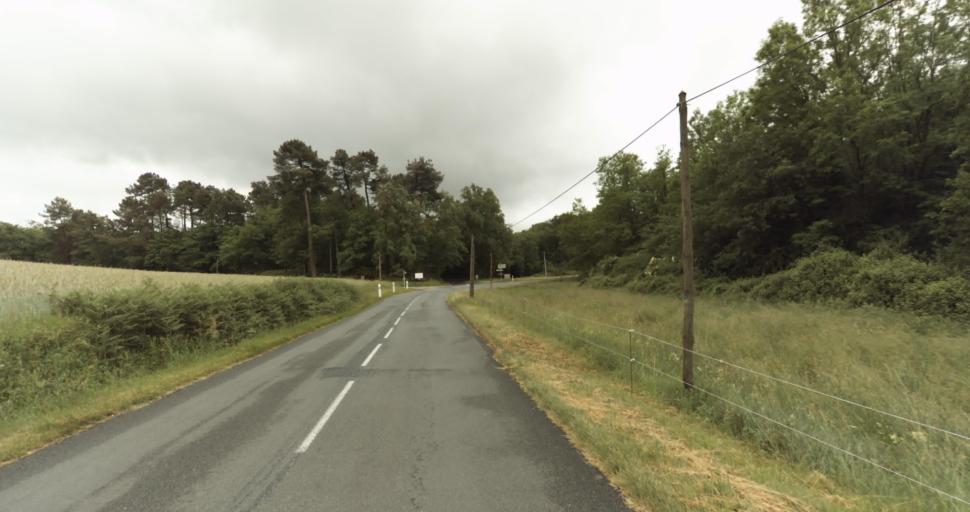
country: FR
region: Aquitaine
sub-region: Departement de la Dordogne
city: Belves
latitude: 44.7099
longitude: 0.9343
